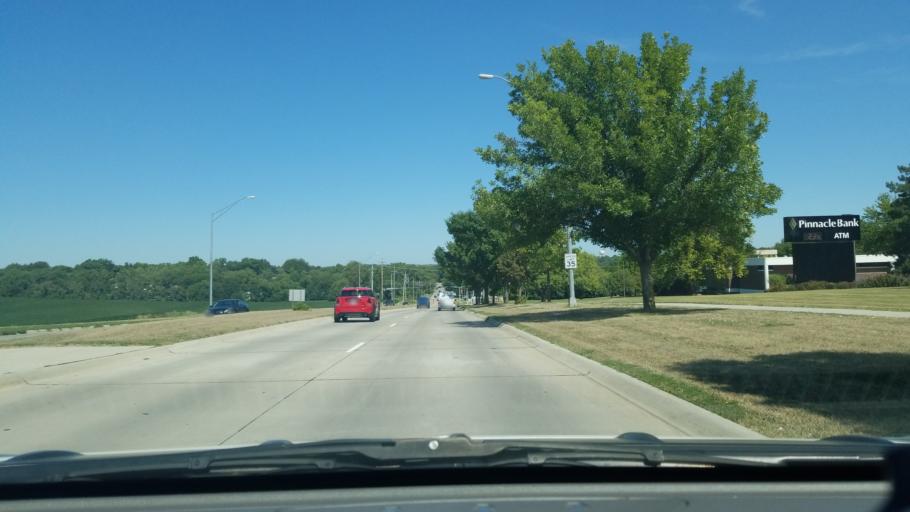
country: US
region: Nebraska
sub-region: Sarpy County
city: Papillion
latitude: 41.1413
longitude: -96.0428
